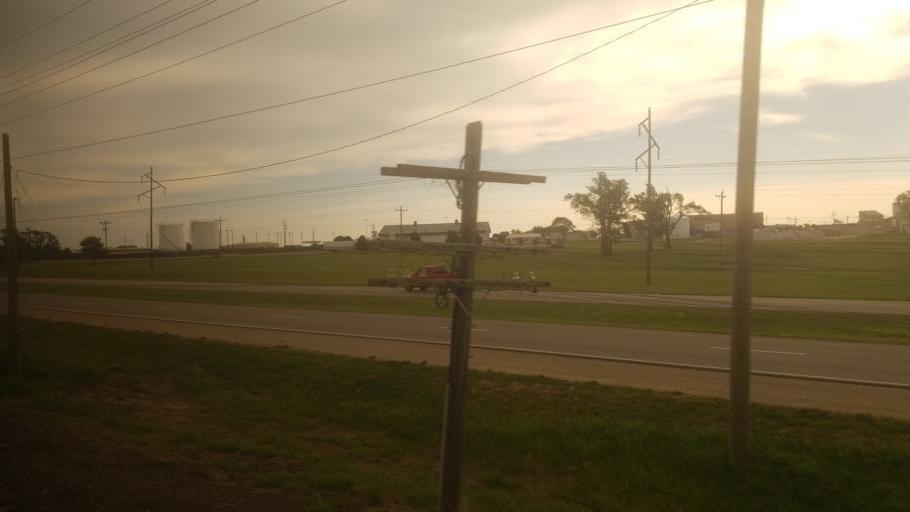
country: US
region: Kansas
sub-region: Shawnee County
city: Topeka
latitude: 38.9550
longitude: -95.6877
